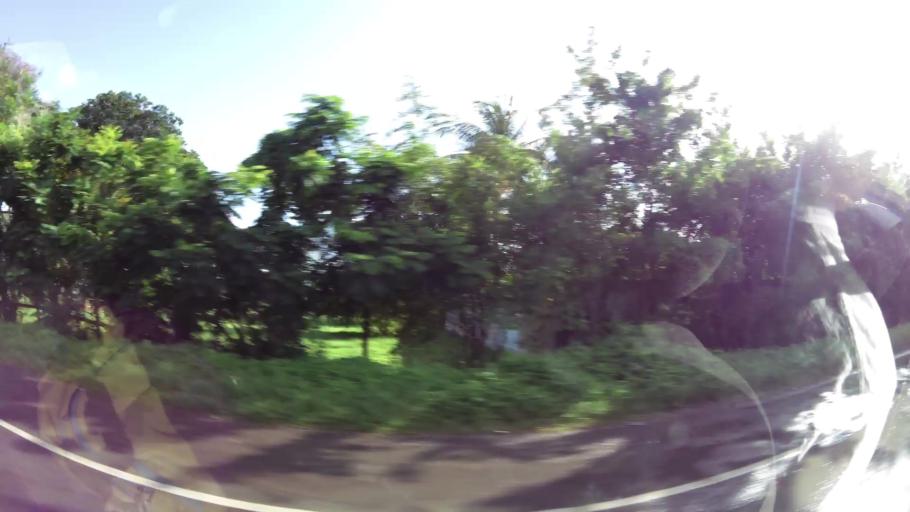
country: GY
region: Demerara-Mahaica
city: Georgetown
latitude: 6.8212
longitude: -58.0967
